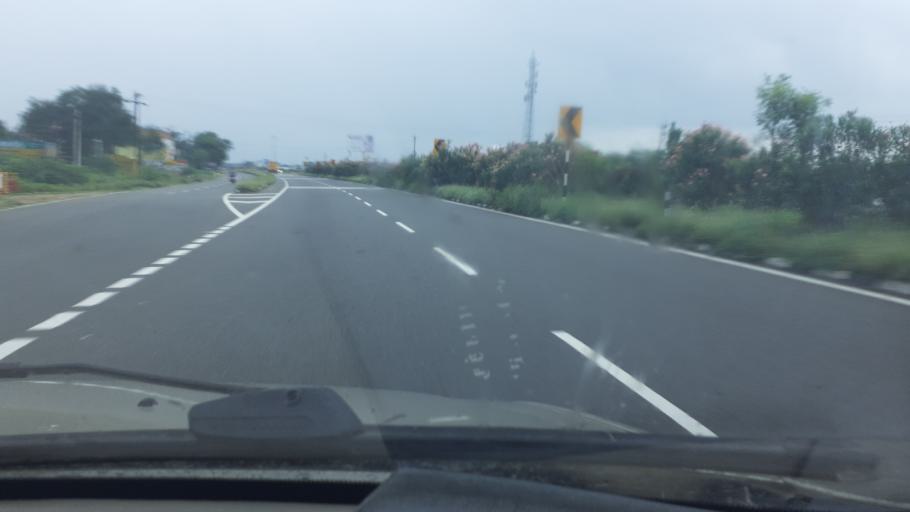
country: IN
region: Tamil Nadu
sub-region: Virudhunagar
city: Virudunagar
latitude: 9.6267
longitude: 77.9588
